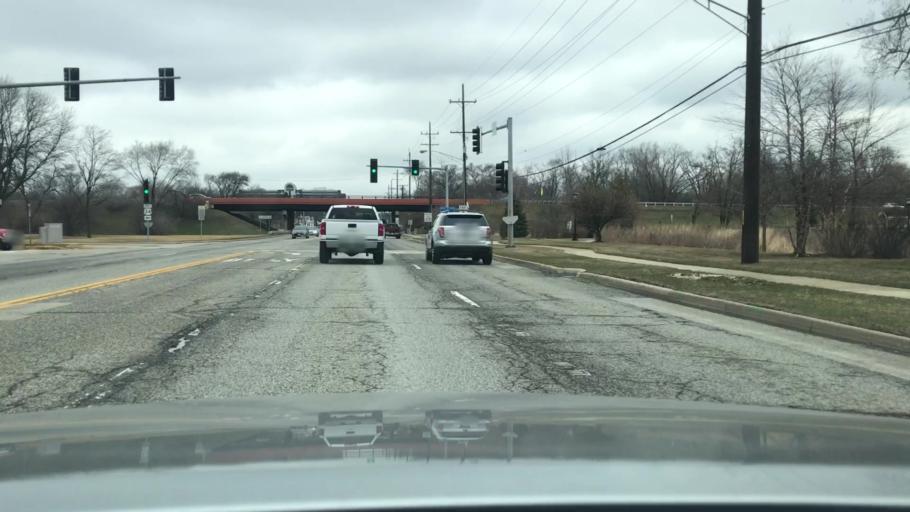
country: US
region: Illinois
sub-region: DuPage County
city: Lisle
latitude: 41.7995
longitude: -88.0774
